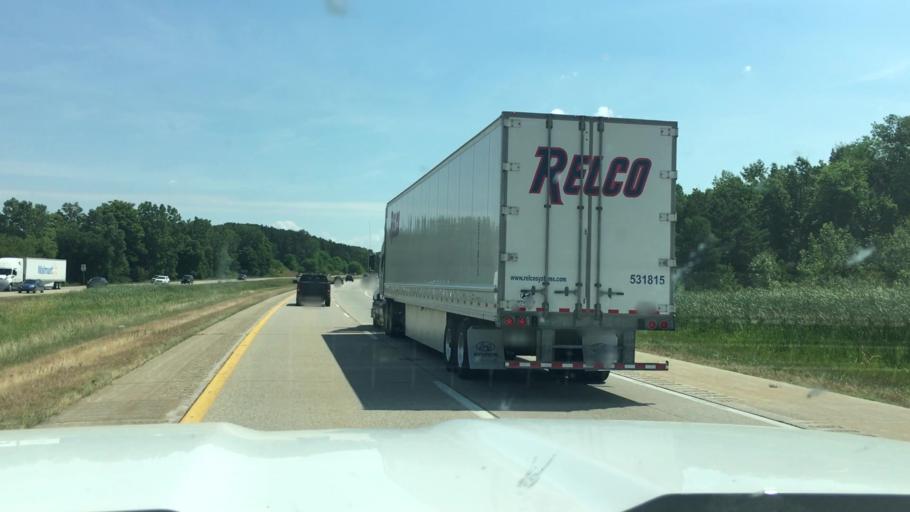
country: US
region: Michigan
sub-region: Shiawassee County
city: Perry
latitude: 42.8379
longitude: -84.2313
